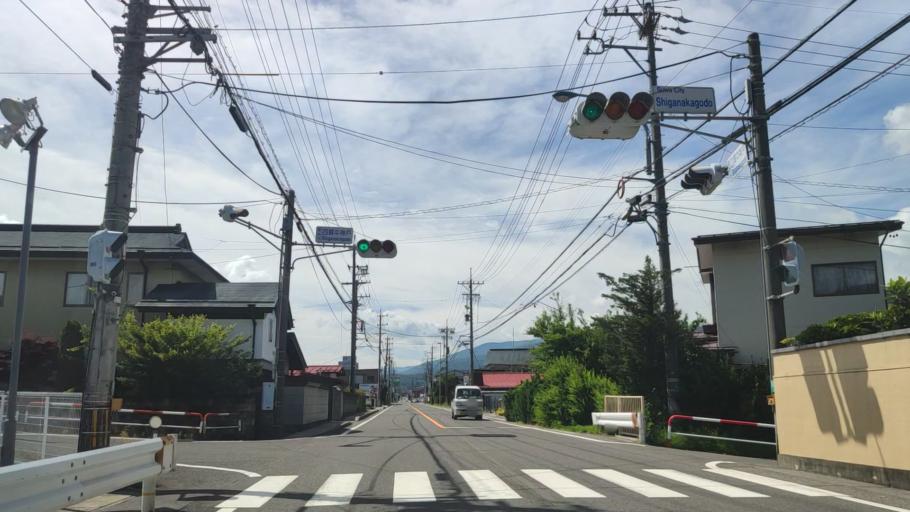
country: JP
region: Nagano
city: Chino
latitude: 36.0135
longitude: 138.1368
